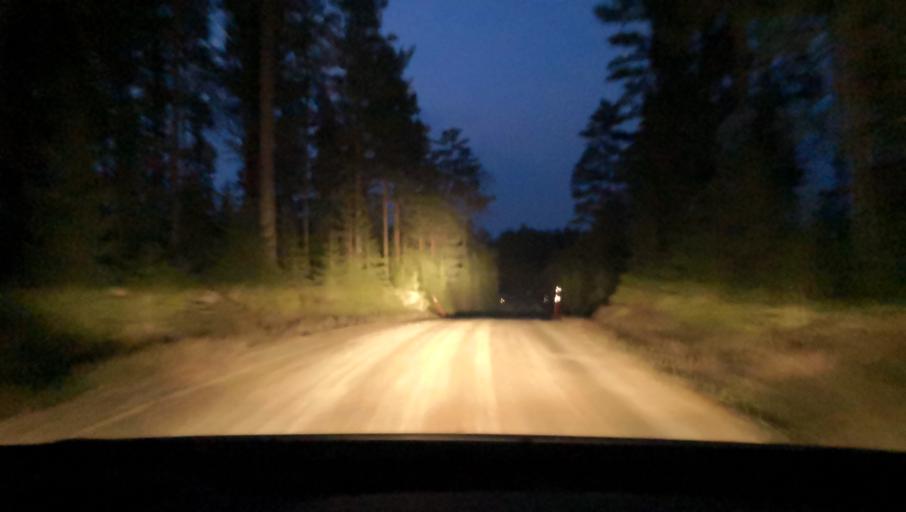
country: SE
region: OErebro
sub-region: Lindesbergs Kommun
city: Frovi
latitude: 59.6490
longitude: 15.4862
